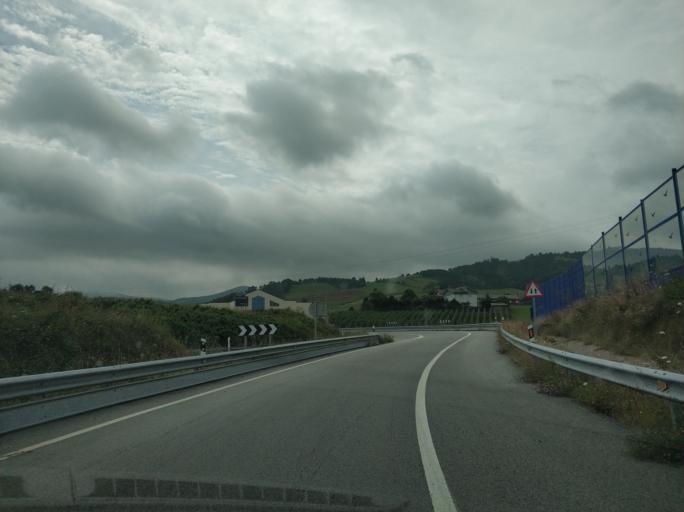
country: ES
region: Asturias
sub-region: Province of Asturias
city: Navia
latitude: 43.5279
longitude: -6.5545
